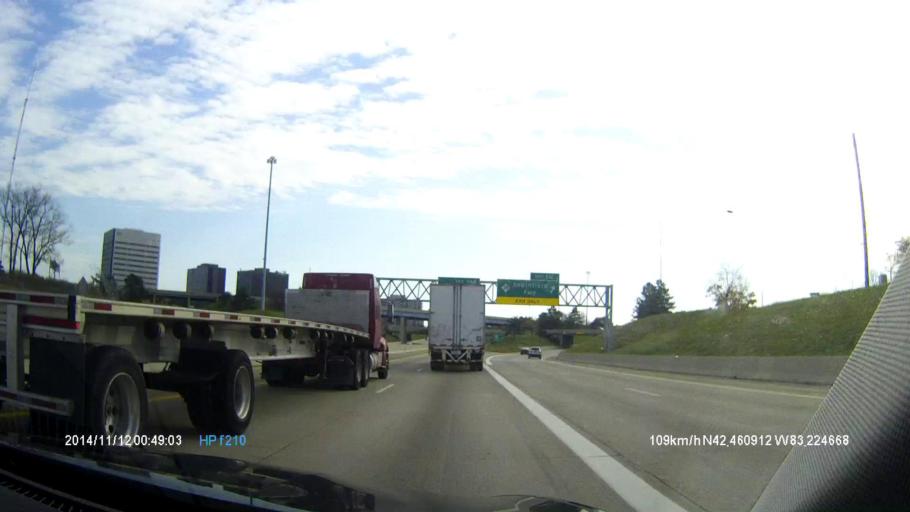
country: US
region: Michigan
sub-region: Oakland County
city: Southfield
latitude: 42.4607
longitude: -83.2244
